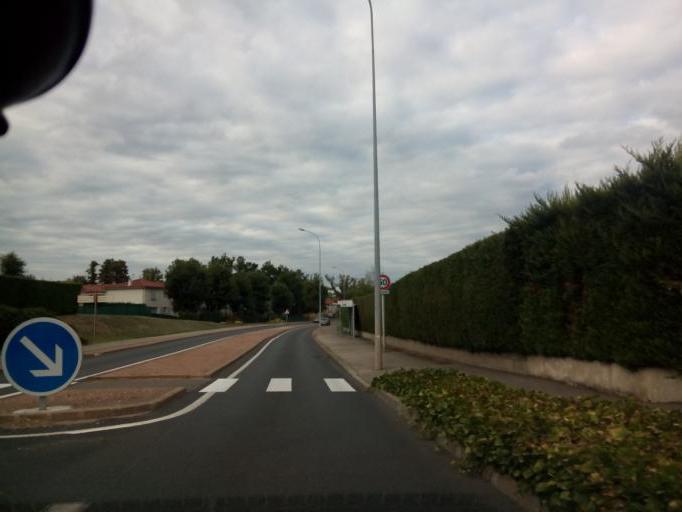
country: FR
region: Rhone-Alpes
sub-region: Departement du Rhone
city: Sainte-Consorce
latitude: 45.7877
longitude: 4.7071
